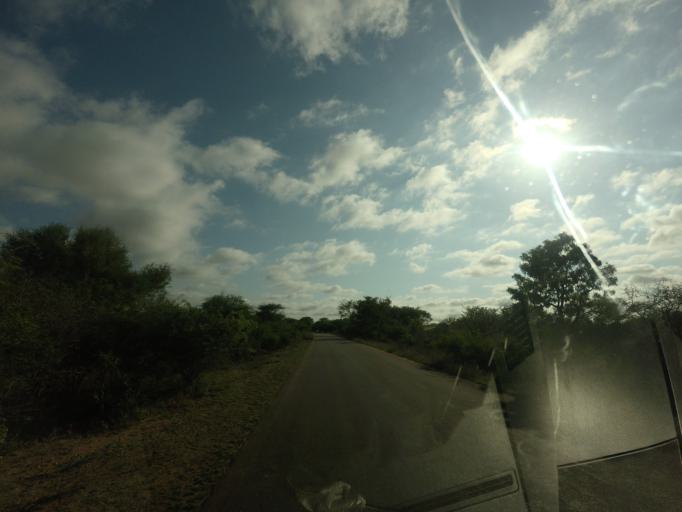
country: ZA
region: Mpumalanga
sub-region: Ehlanzeni District
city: Komatipoort
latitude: -25.2265
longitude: 31.8569
